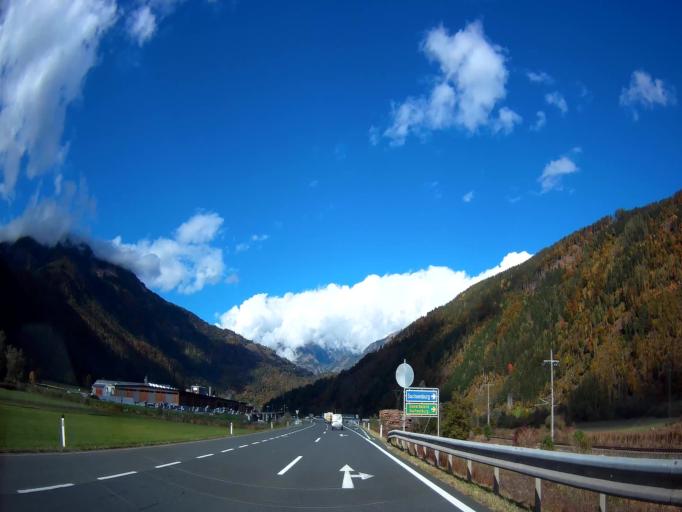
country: AT
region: Carinthia
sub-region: Politischer Bezirk Spittal an der Drau
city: Sachsenburg
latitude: 46.8079
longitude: 13.3556
